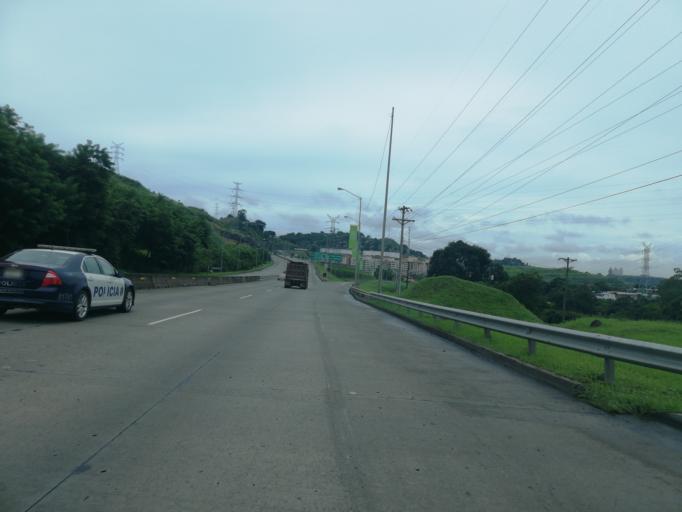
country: PA
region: Panama
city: Las Cumbres
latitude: 9.0558
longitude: -79.5153
